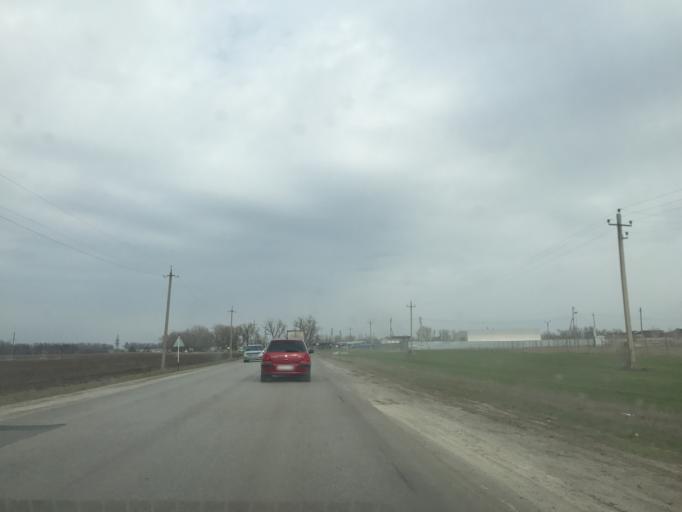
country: RU
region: Rostov
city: Starocherkasskaya
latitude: 47.3168
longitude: 39.9640
